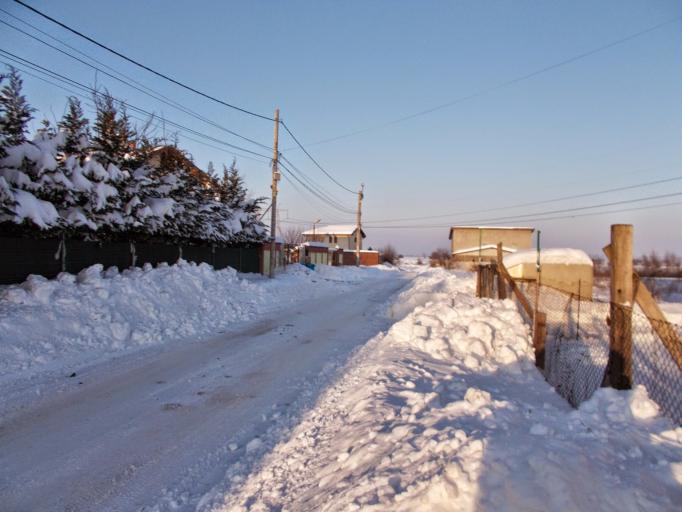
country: RO
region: Ilfov
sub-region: Comuna Berceni
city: Berceni
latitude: 44.3269
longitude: 26.1765
